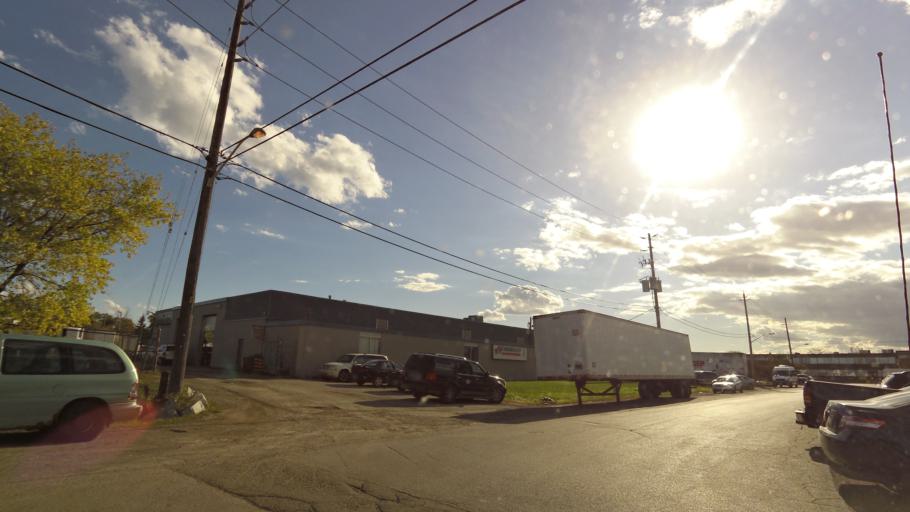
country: CA
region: Ontario
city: Etobicoke
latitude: 43.6022
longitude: -79.5271
